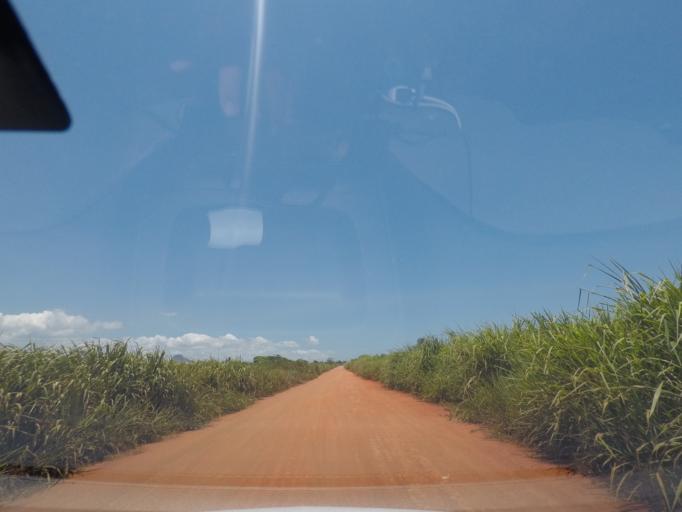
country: BR
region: Rio de Janeiro
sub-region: Niteroi
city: Niteroi
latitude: -22.9682
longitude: -42.9958
